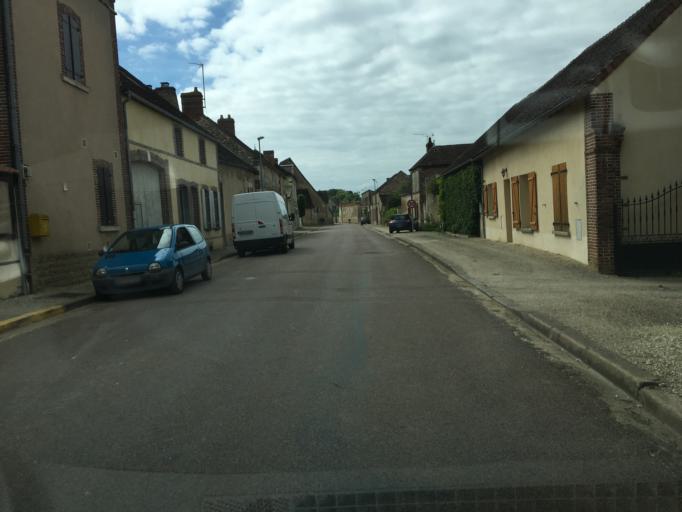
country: FR
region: Bourgogne
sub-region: Departement de l'Yonne
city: Laroche-Saint-Cydroine
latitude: 47.9514
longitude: 3.4393
